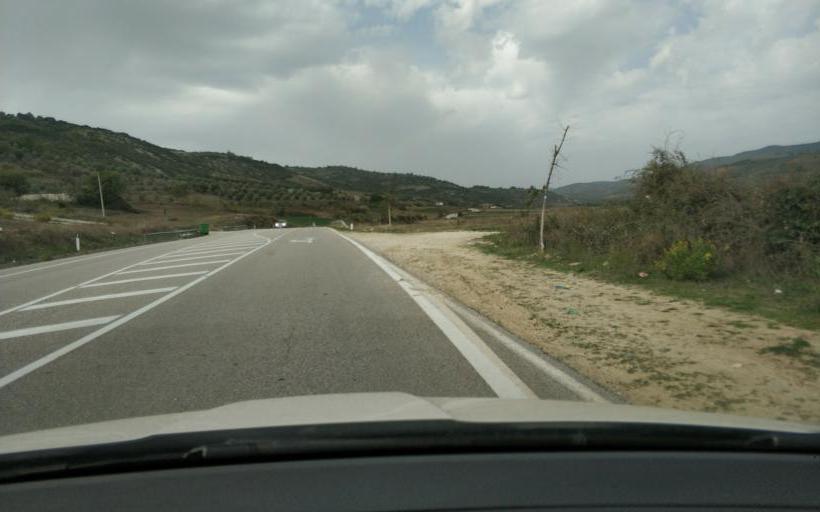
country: AL
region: Gjirokaster
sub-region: Rrethi i Tepelenes
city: Krahes
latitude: 40.4399
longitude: 19.8490
